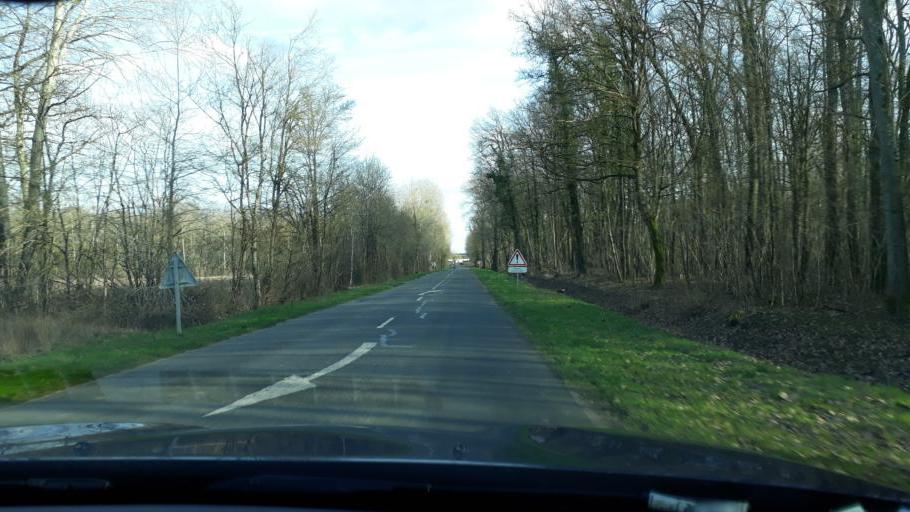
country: FR
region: Centre
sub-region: Departement du Loiret
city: Chilleurs-aux-Bois
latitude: 48.0620
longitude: 2.1582
